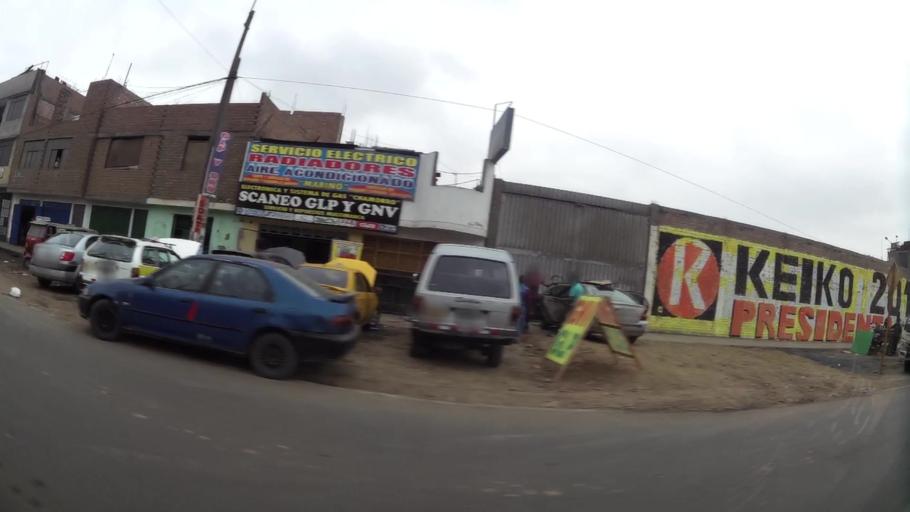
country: PE
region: Lima
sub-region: Lima
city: Vitarte
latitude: -12.0426
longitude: -76.9600
